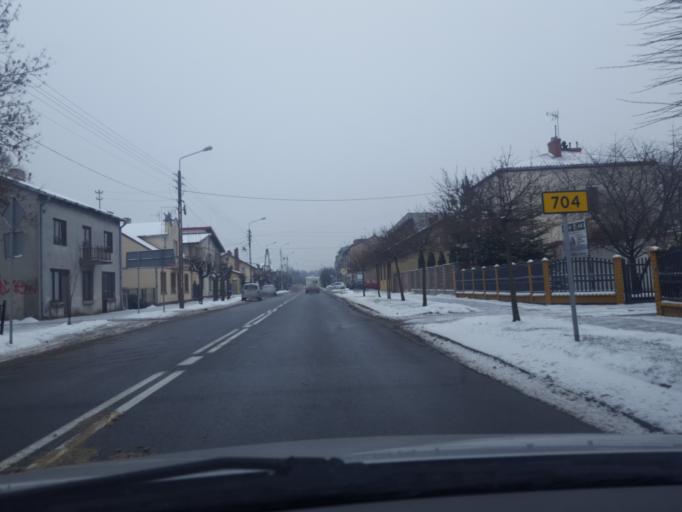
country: PL
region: Lodz Voivodeship
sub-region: powiat Lowicki
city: Lyszkowice
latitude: 51.9858
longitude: 19.9065
